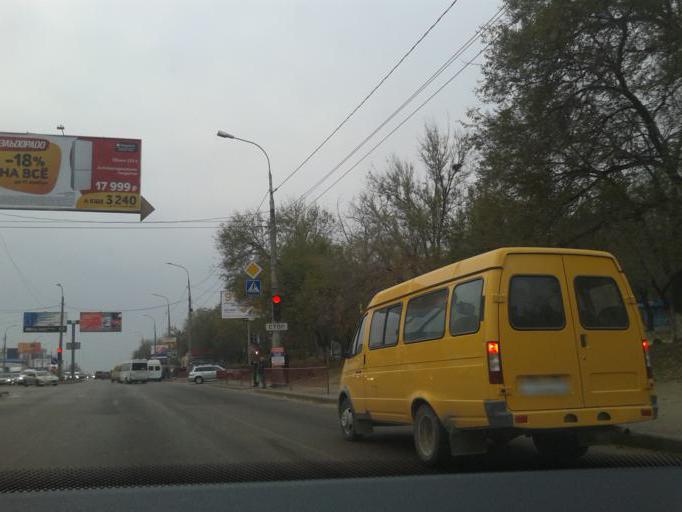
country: RU
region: Volgograd
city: Volgograd
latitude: 48.6760
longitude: 44.4441
